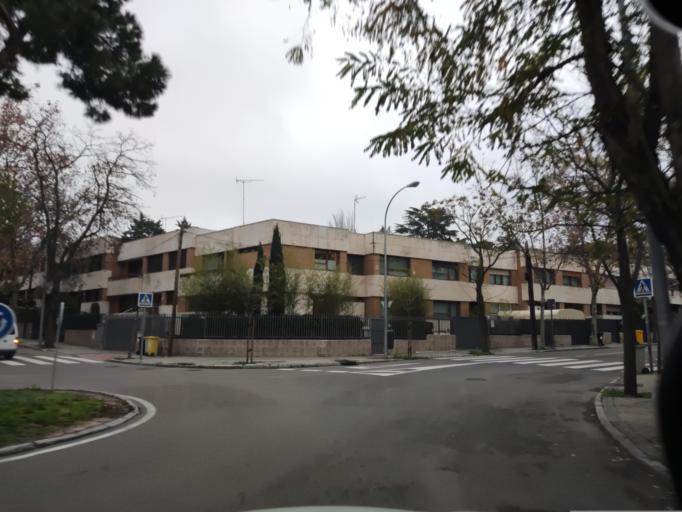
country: ES
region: Madrid
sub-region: Provincia de Madrid
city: Fuencarral-El Pardo
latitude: 40.4930
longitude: -3.7107
